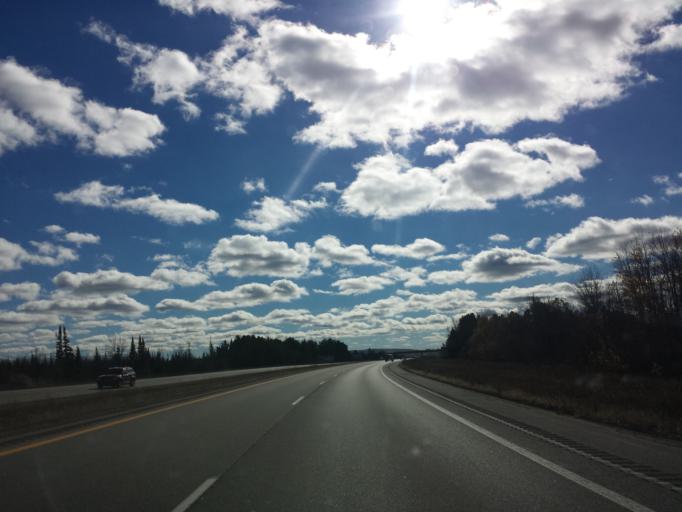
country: US
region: Michigan
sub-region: Cheboygan County
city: Indian River
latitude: 45.4168
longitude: -84.6025
